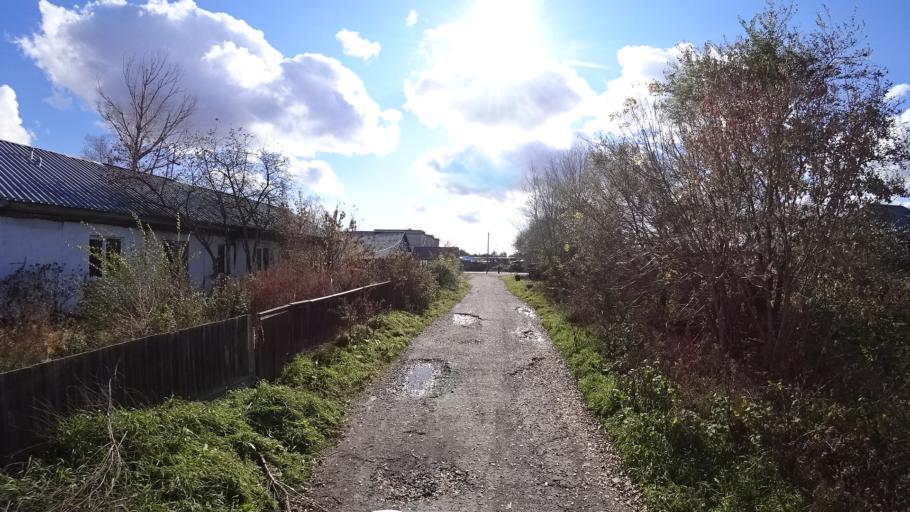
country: RU
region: Khabarovsk Krai
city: Amursk
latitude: 50.0993
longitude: 136.5008
